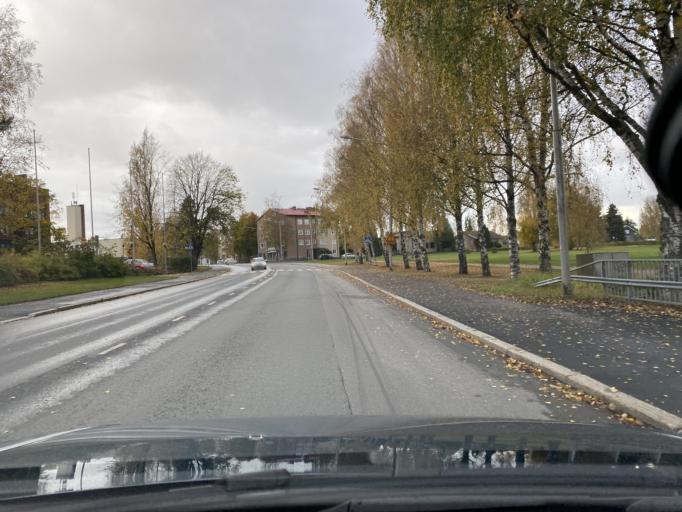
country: FI
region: Haeme
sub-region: Forssa
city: Forssa
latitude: 60.8148
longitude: 23.6182
